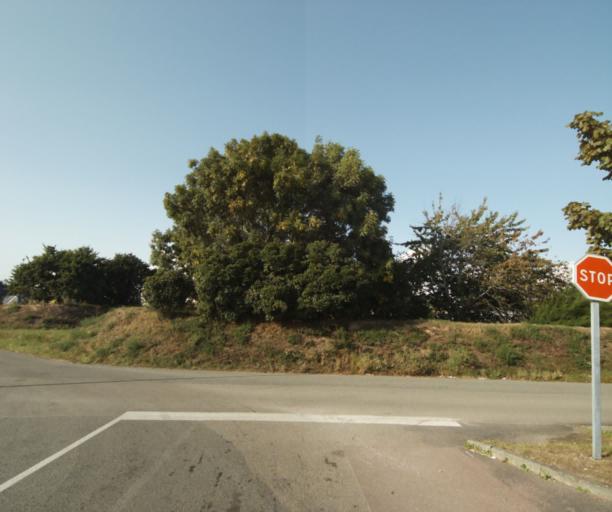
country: FR
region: Brittany
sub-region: Departement du Morbihan
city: Locmiquelic
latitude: 47.7190
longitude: -3.3347
